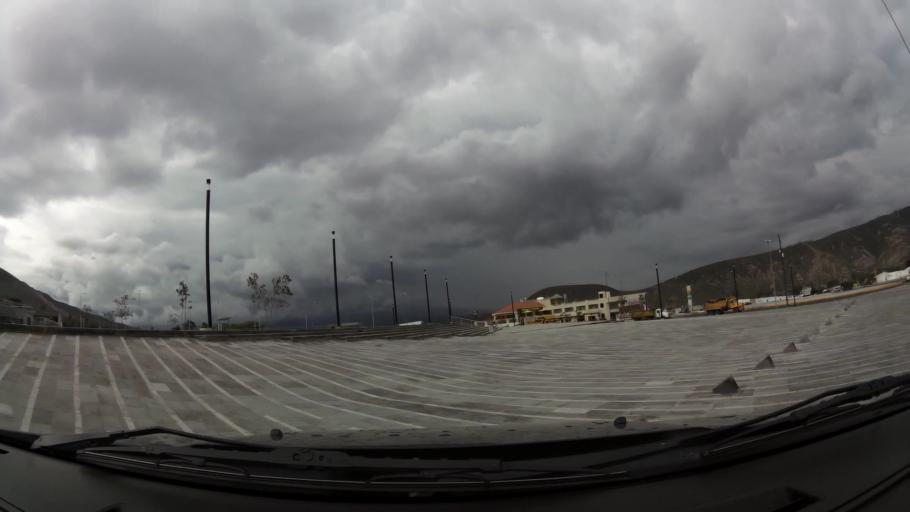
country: EC
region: Pichincha
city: Quito
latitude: -0.0037
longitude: -78.4539
